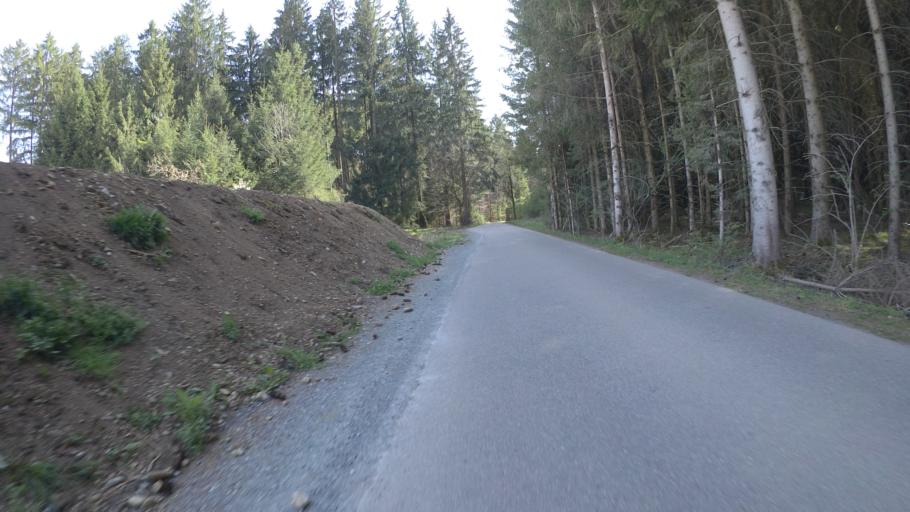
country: DE
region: Bavaria
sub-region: Upper Bavaria
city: Nussdorf
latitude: 47.9016
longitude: 12.6132
